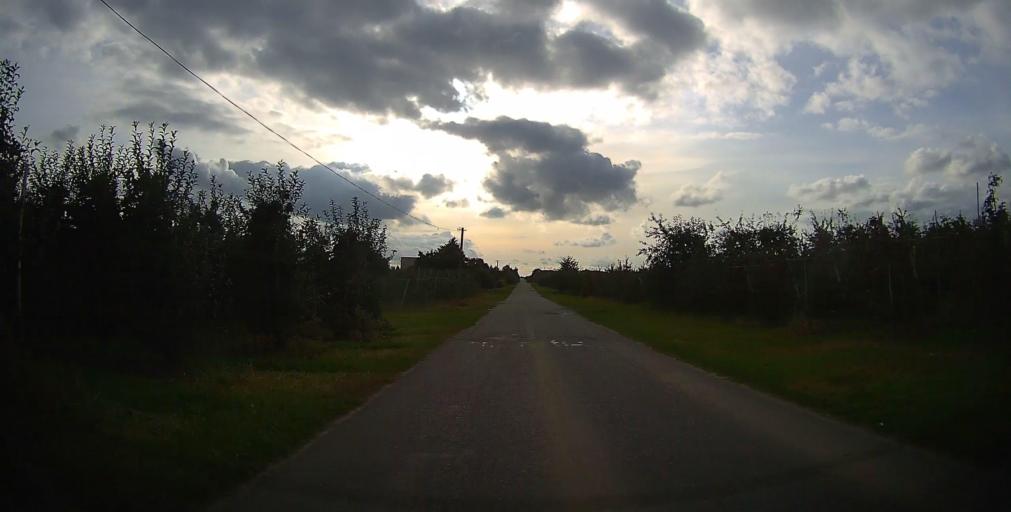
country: PL
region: Masovian Voivodeship
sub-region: Powiat grojecki
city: Jasieniec
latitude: 51.7702
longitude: 20.9126
